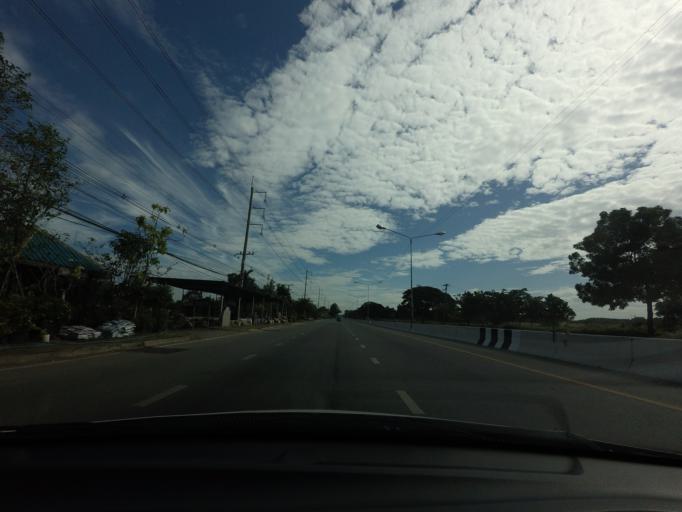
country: TH
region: Pathum Thani
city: Nong Suea
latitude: 14.0817
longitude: 100.9067
